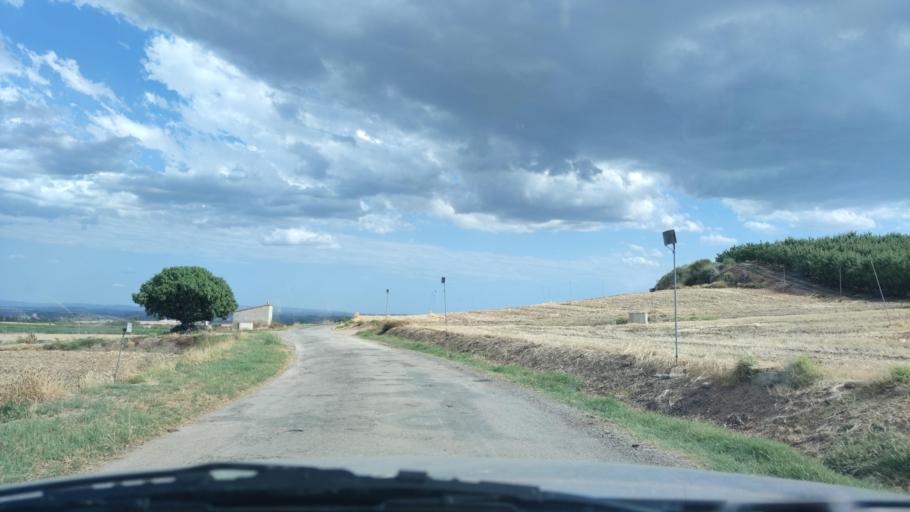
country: ES
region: Catalonia
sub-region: Provincia de Lleida
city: Alcarras
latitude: 41.5944
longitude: 0.5416
